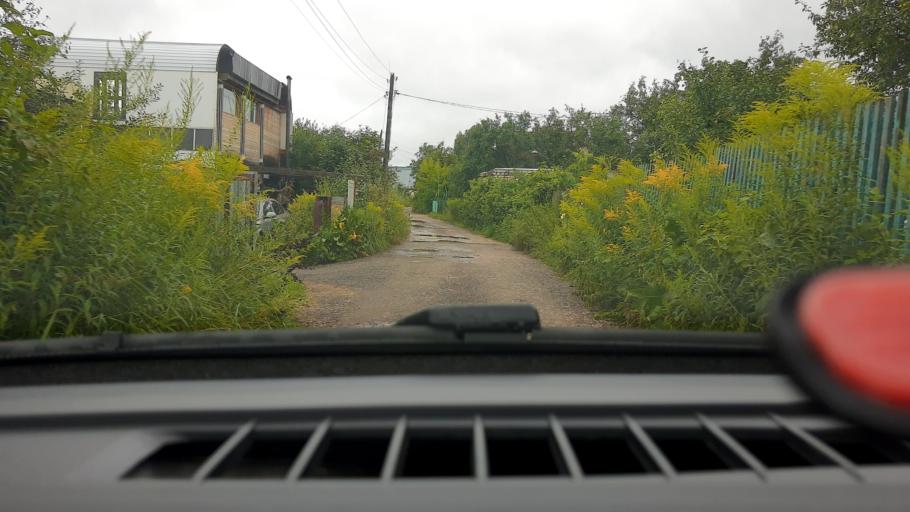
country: RU
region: Nizjnij Novgorod
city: Gorbatovka
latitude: 56.3164
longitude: 43.8361
